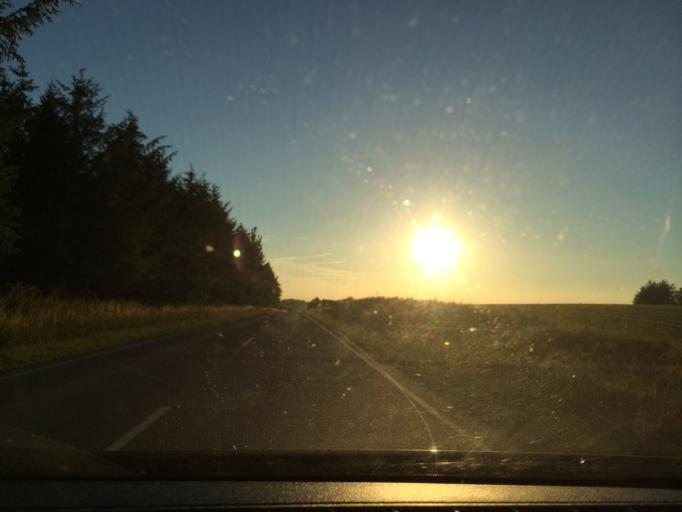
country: DK
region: Zealand
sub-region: Vordingborg Kommune
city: Praesto
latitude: 55.0098
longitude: 12.1317
